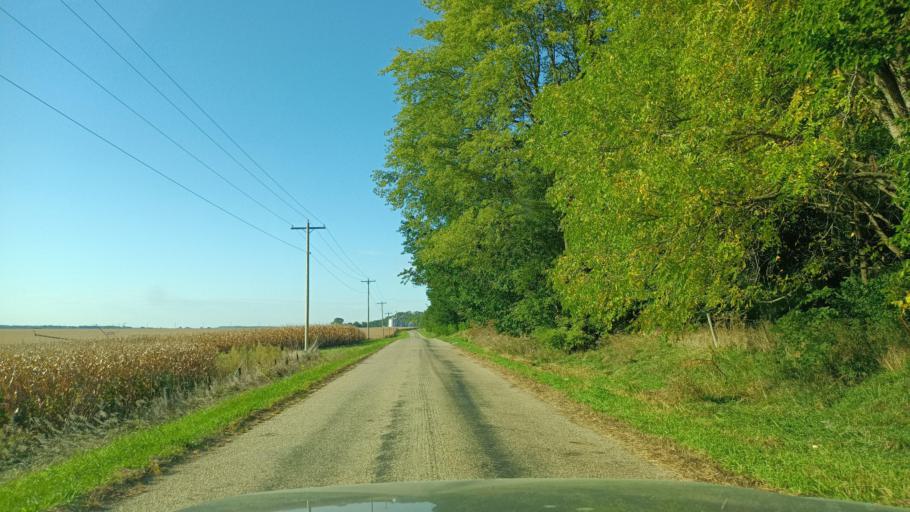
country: US
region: Illinois
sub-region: Mercer County
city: Aledo
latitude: 41.1739
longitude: -90.9190
